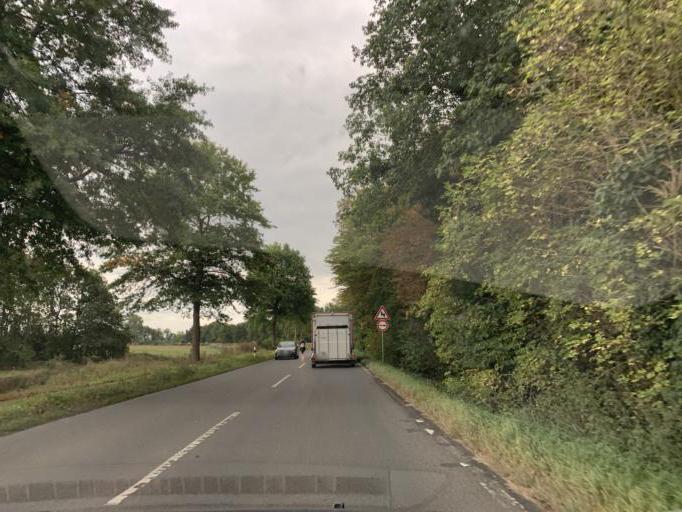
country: DE
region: North Rhine-Westphalia
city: Huckelhoven
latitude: 51.0294
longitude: 6.2204
